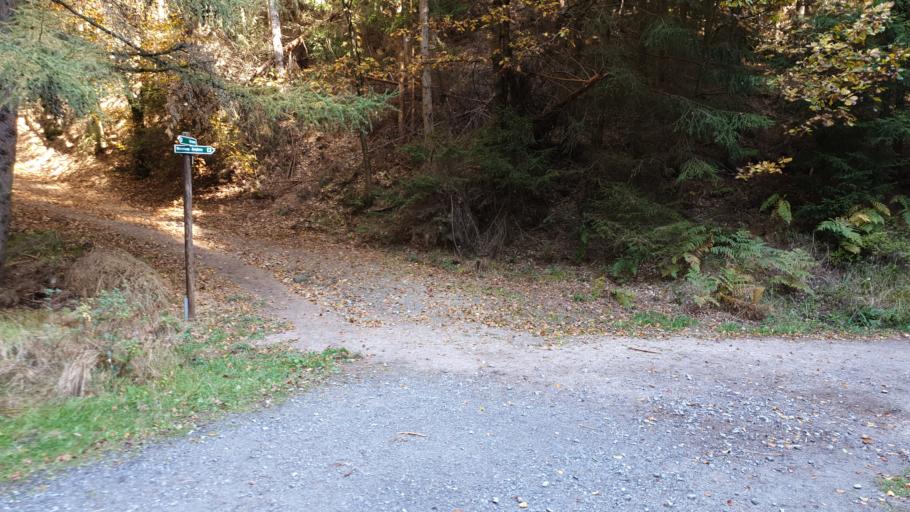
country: DE
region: Saxony
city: Bad Schandau
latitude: 50.9020
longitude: 14.2355
